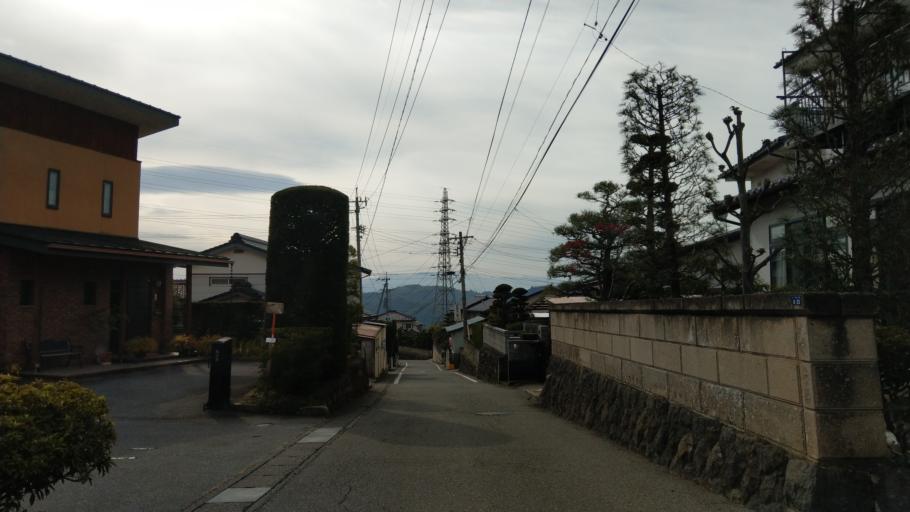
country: JP
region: Nagano
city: Komoro
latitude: 36.3329
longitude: 138.4344
